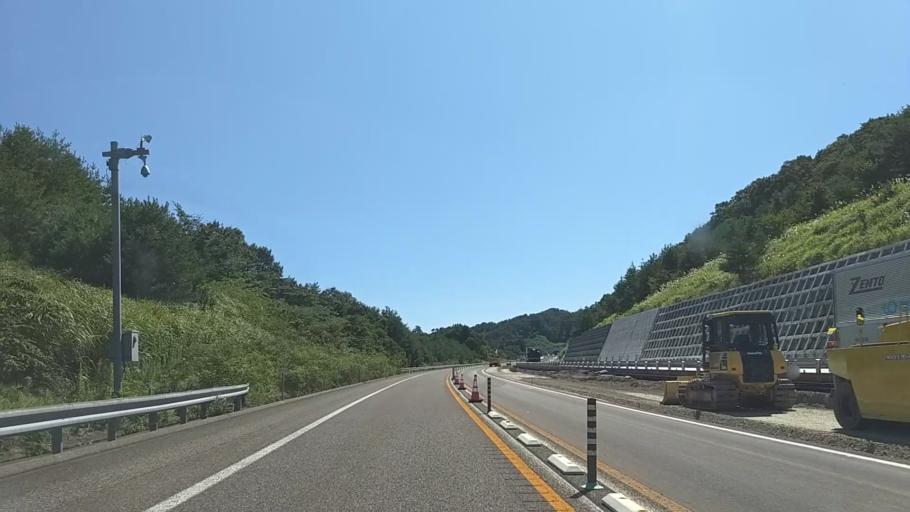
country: JP
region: Niigata
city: Joetsu
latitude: 37.1151
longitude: 138.2180
